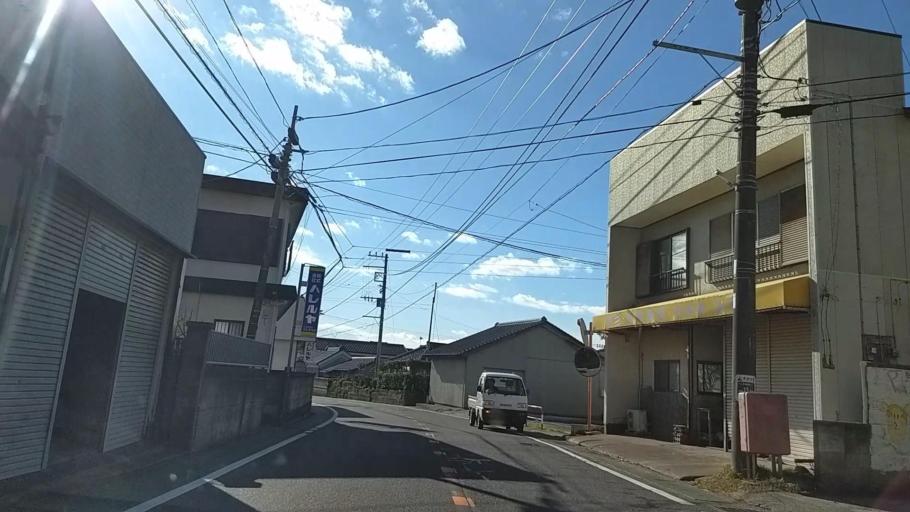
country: JP
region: Chiba
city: Tateyama
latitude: 35.0625
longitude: 139.8271
